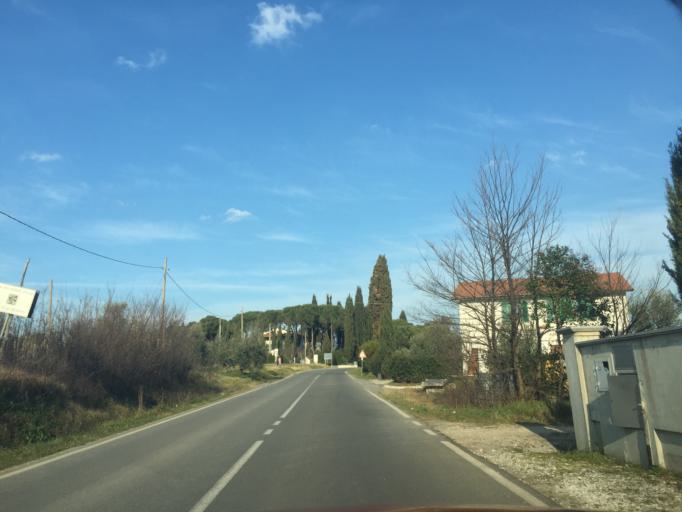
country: IT
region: Tuscany
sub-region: Province of Florence
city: Cerreto Guidi
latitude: 43.7627
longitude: 10.8831
